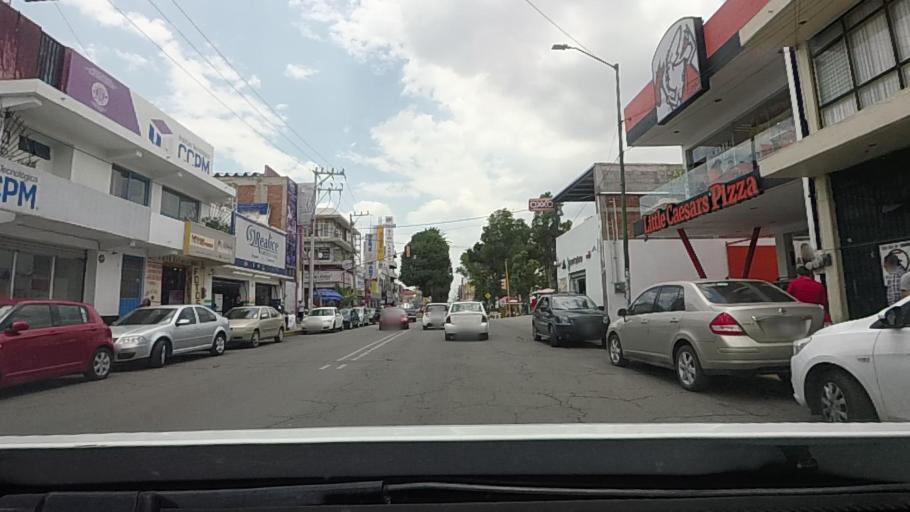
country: MX
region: Mexico
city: Chalco de Diaz Covarrubias
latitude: 19.2606
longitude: -98.8962
